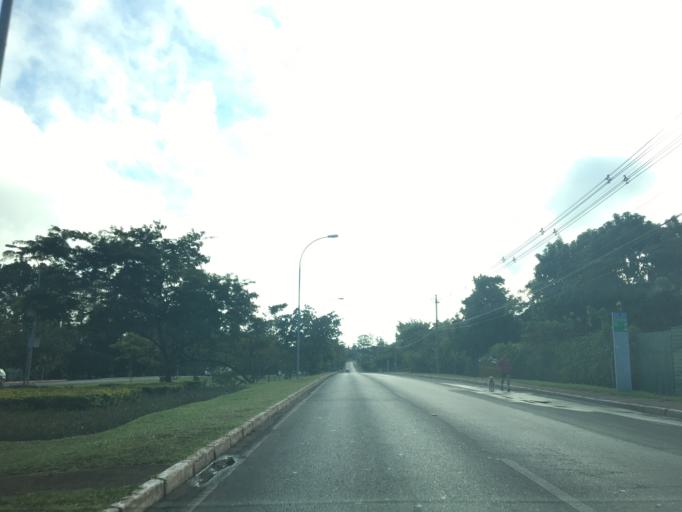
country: BR
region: Federal District
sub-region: Brasilia
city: Brasilia
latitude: -15.8294
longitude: -47.8107
